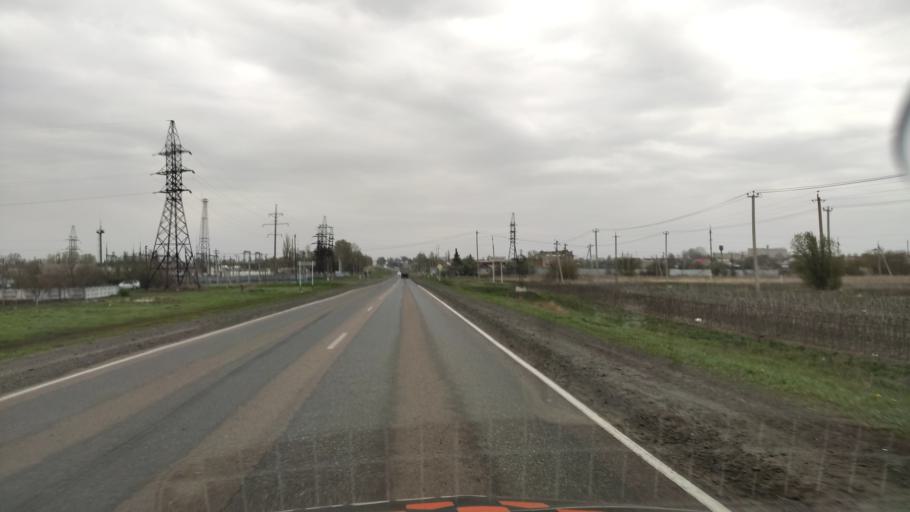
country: RU
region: Kursk
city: Gorshechnoye
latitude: 51.5141
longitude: 38.0081
